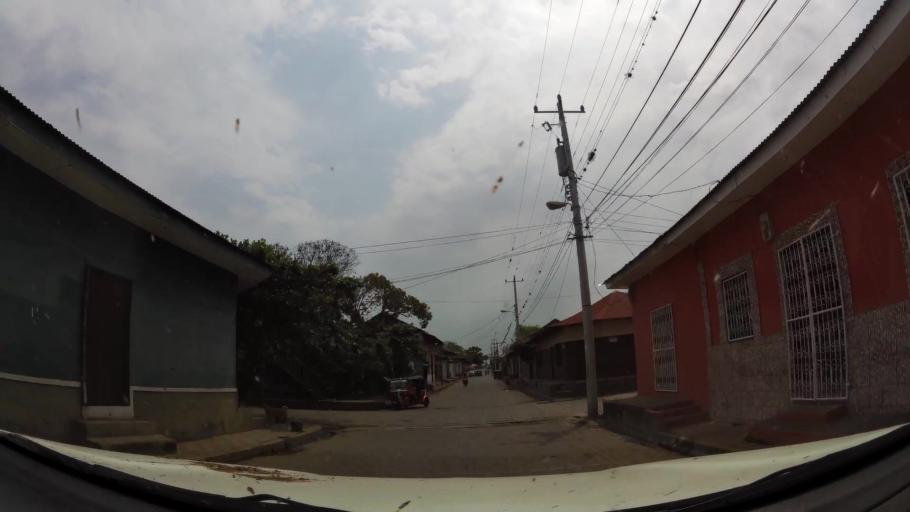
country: NI
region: Granada
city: Diriomo
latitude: 11.8752
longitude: -86.0500
